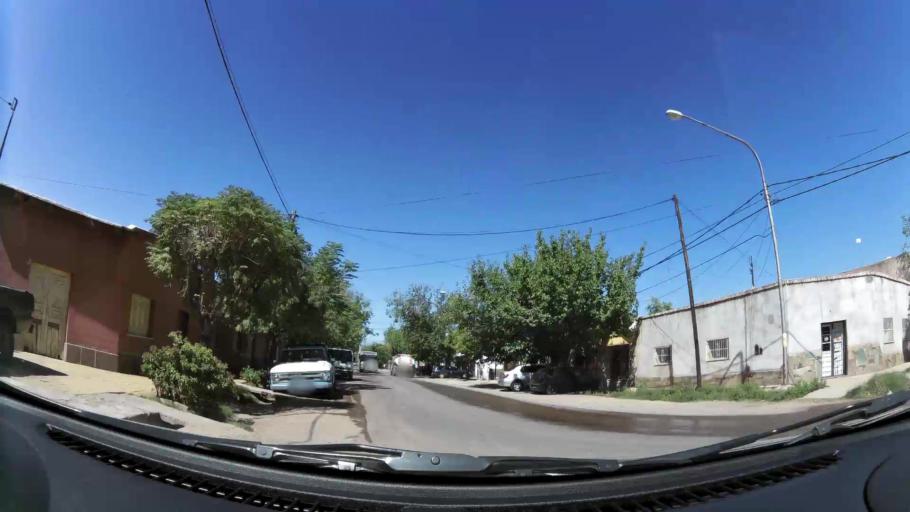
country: AR
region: Mendoza
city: Mendoza
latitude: -32.8930
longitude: -68.8041
